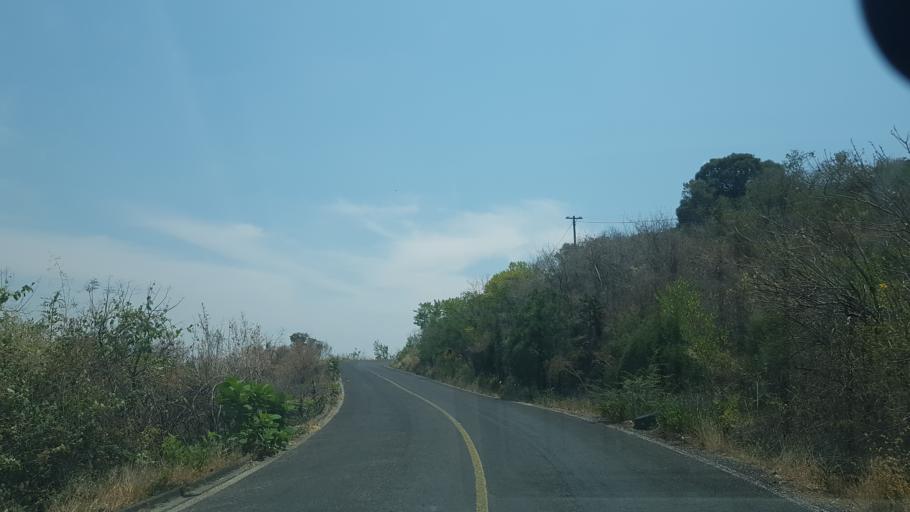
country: MX
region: Puebla
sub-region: Atzitzihuacan
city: Santiago Atzitzihuacan
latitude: 18.8379
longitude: -98.5877
